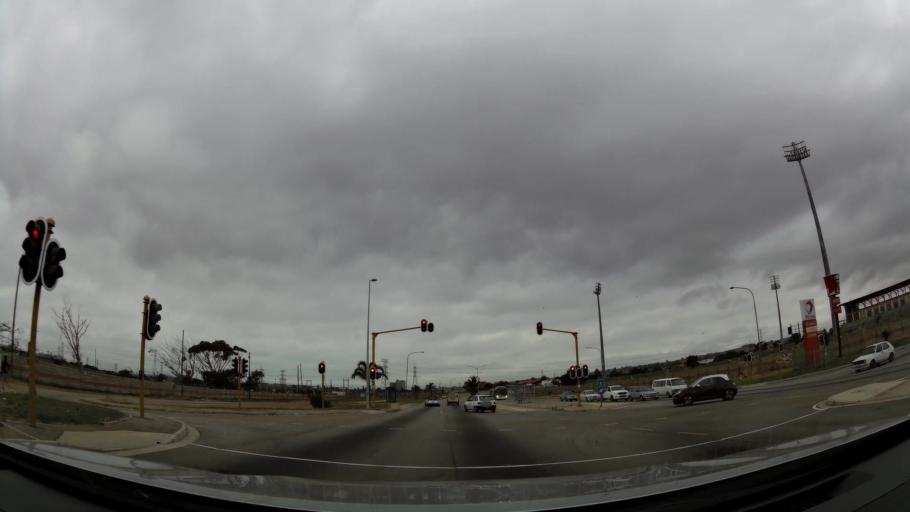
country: ZA
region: Eastern Cape
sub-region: Nelson Mandela Bay Metropolitan Municipality
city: Port Elizabeth
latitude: -33.9126
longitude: 25.5606
